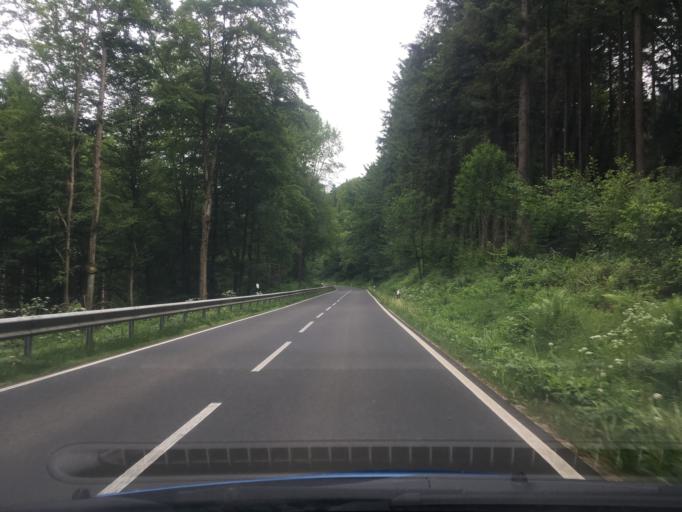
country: DE
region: Lower Saxony
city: Dassel
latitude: 51.7537
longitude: 9.6681
